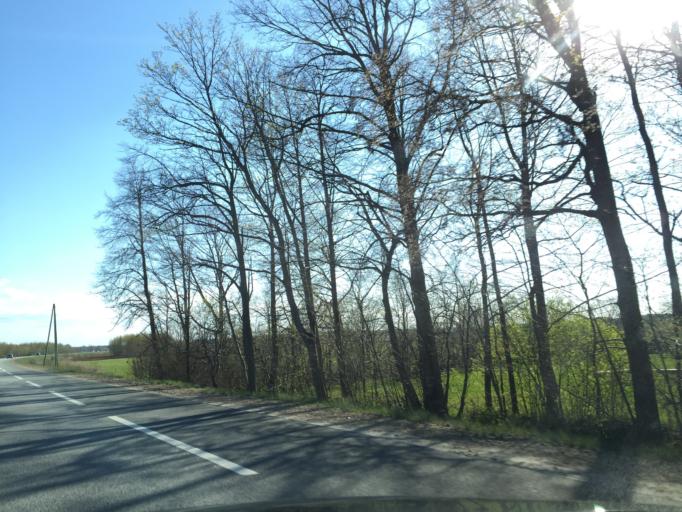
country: LV
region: Adazi
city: Adazi
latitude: 57.1149
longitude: 24.3229
